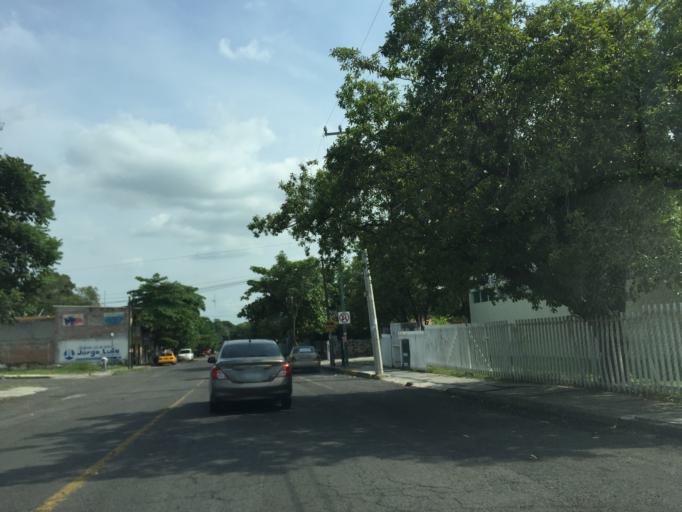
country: MX
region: Colima
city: Colima
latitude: 19.2333
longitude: -103.7324
